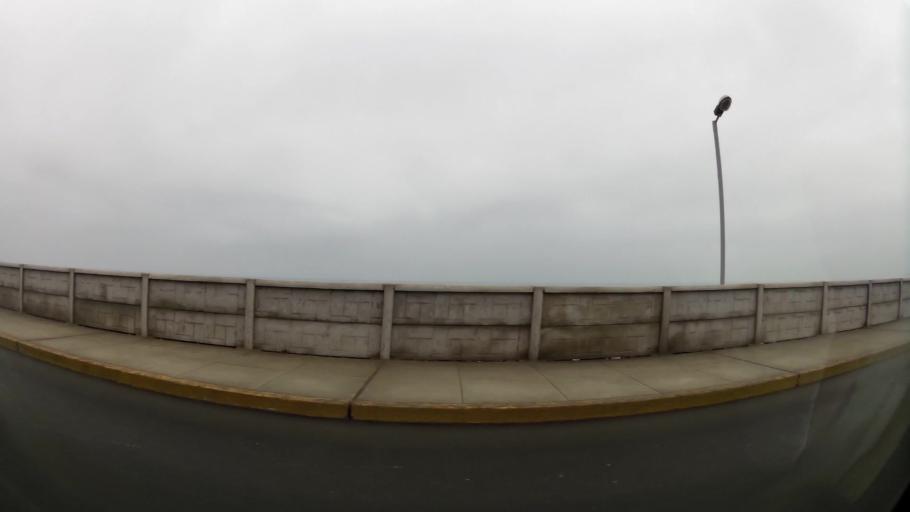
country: PE
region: Callao
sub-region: Callao
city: Callao
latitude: -12.0711
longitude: -77.1299
